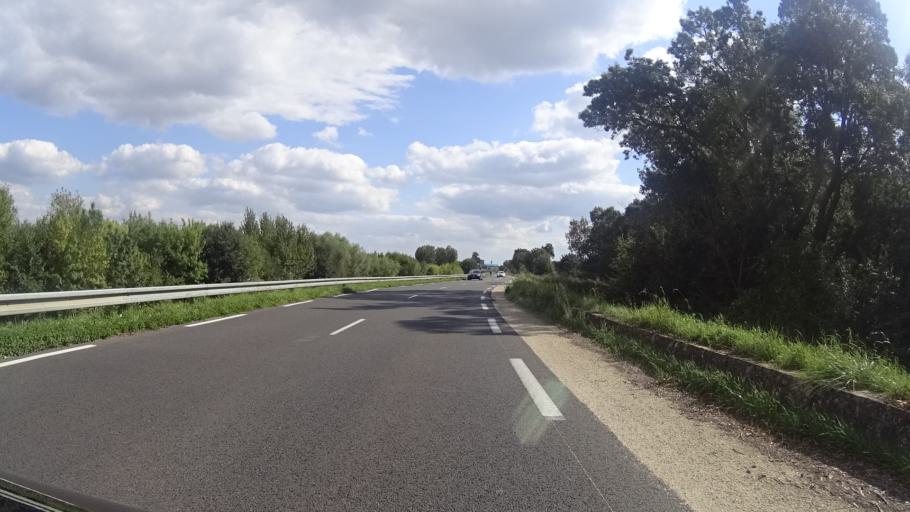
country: FR
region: Pays de la Loire
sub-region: Departement de Maine-et-Loire
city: La Menitre
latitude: 47.4022
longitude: -0.2847
